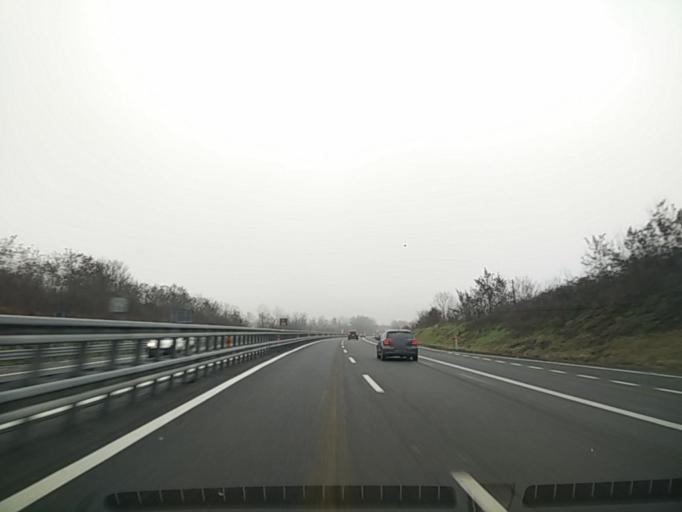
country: IT
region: Piedmont
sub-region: Provincia di Asti
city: Asti
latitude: 44.9135
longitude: 8.1847
